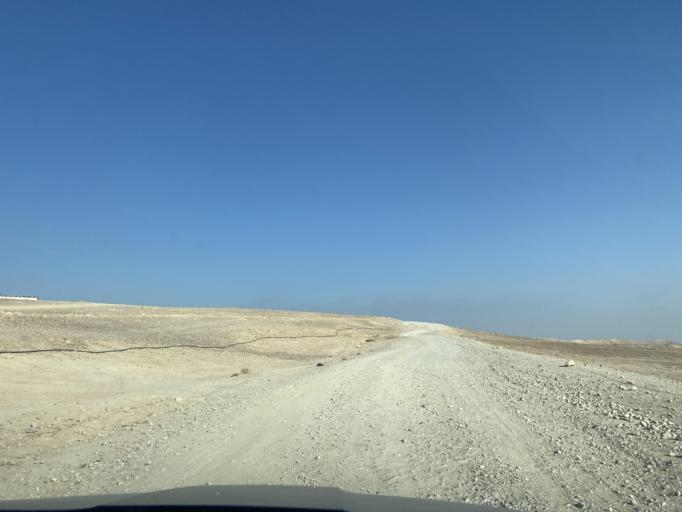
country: PS
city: `Arab ar Rashaydah
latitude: 31.5241
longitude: 35.2986
